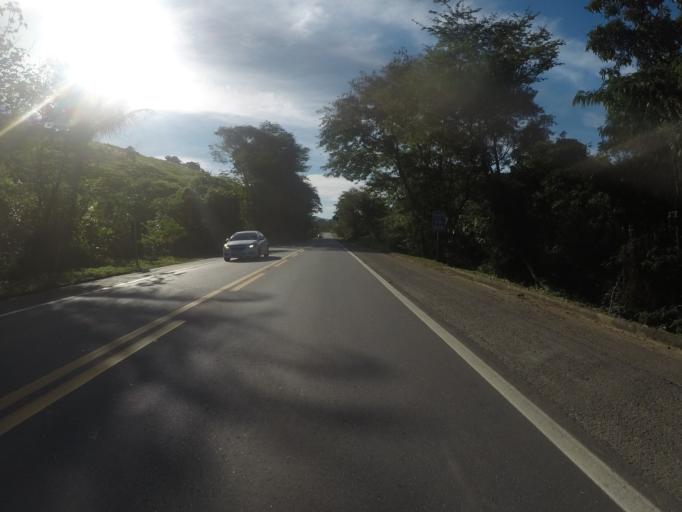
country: BR
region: Espirito Santo
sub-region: Fundao
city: Fundao
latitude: -19.9028
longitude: -40.4084
